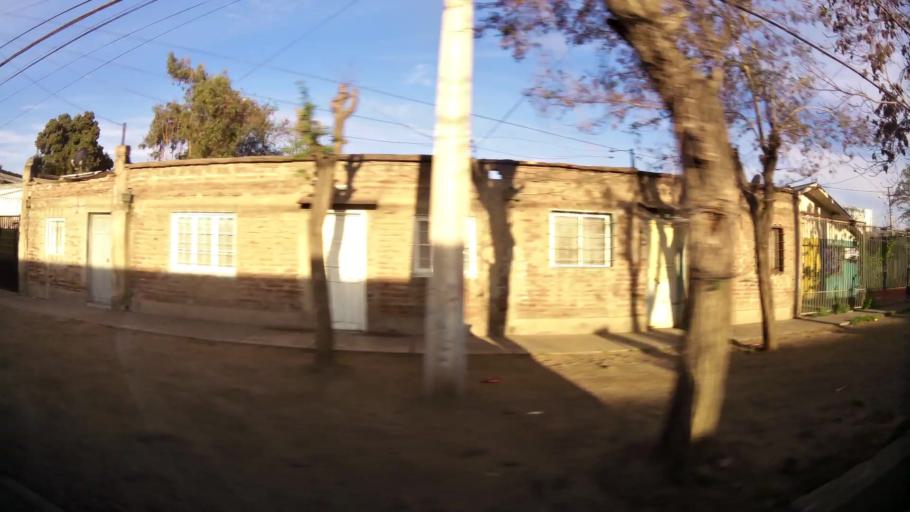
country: CL
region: Santiago Metropolitan
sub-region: Provincia de Santiago
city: Lo Prado
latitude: -33.4264
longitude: -70.7191
